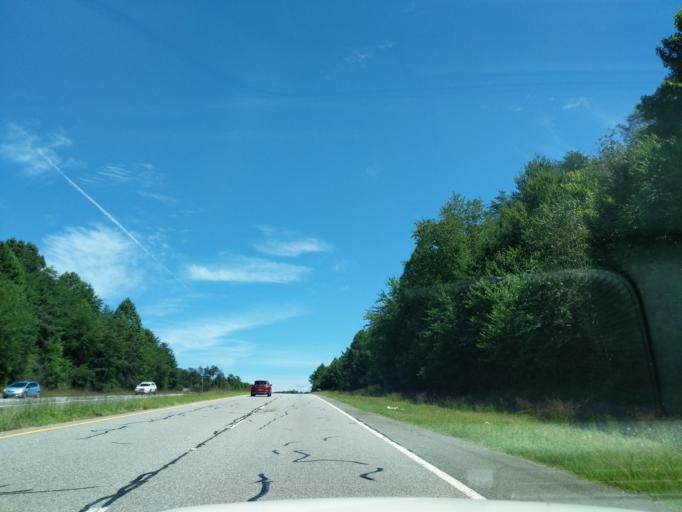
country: US
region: Georgia
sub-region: Fannin County
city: Blue Ridge
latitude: 34.8890
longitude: -84.2201
